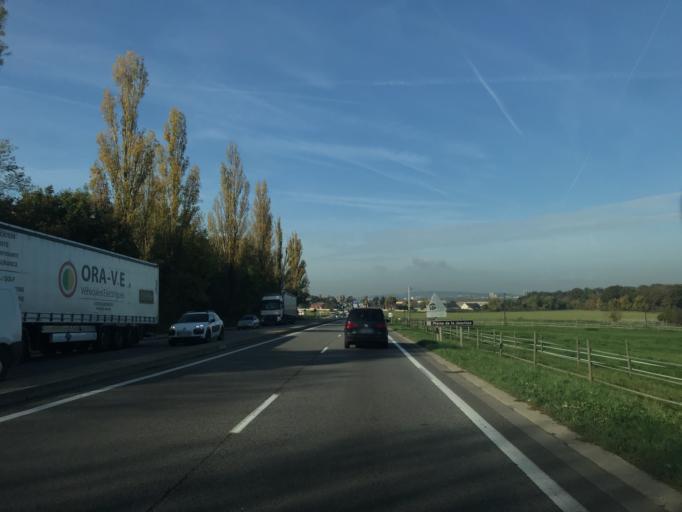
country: FR
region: Ile-de-France
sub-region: Departement des Yvelines
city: Fourqueux
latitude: 48.9011
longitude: 2.0621
